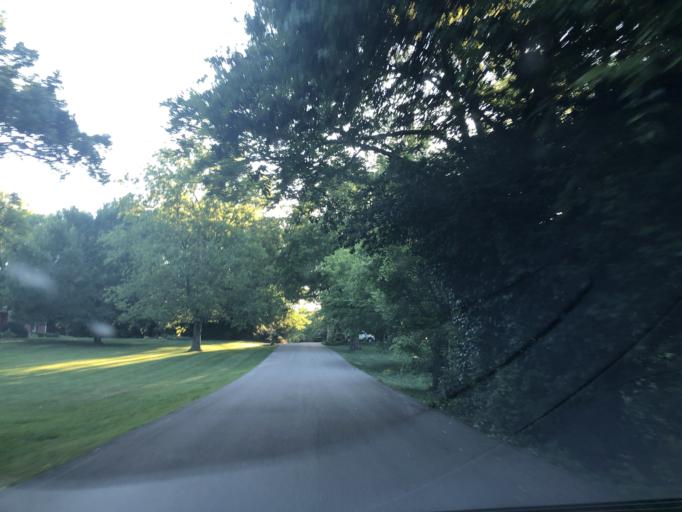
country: US
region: Tennessee
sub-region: Davidson County
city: Oak Hill
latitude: 36.0846
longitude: -86.7996
